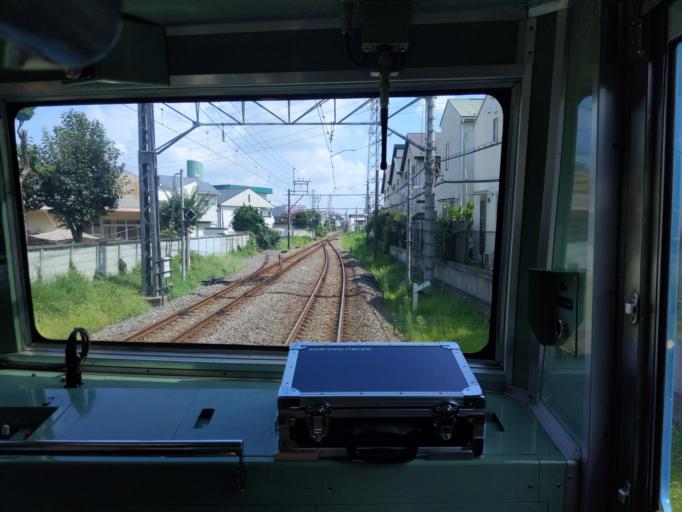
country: JP
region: Tokyo
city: Kamirenjaku
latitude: 35.6964
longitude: 139.5275
